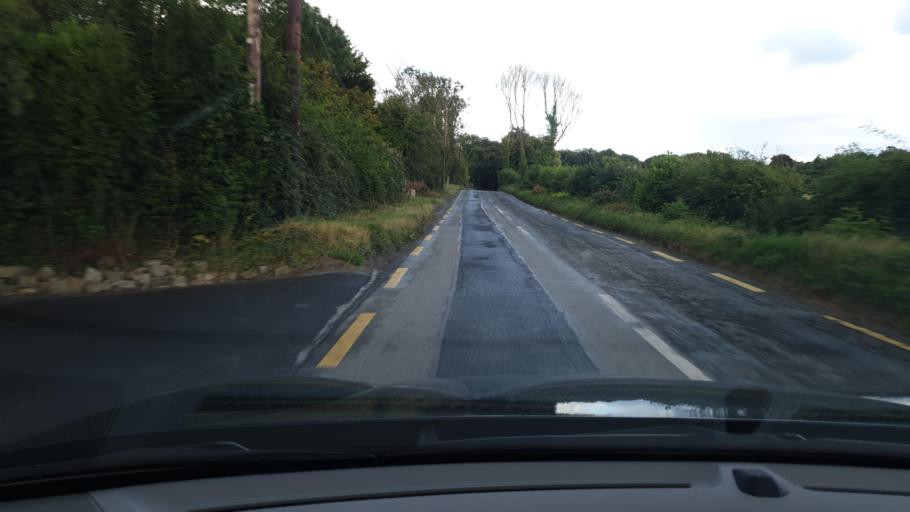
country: IE
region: Leinster
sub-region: South Dublin
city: Rathcoole
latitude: 53.3153
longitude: -6.4567
